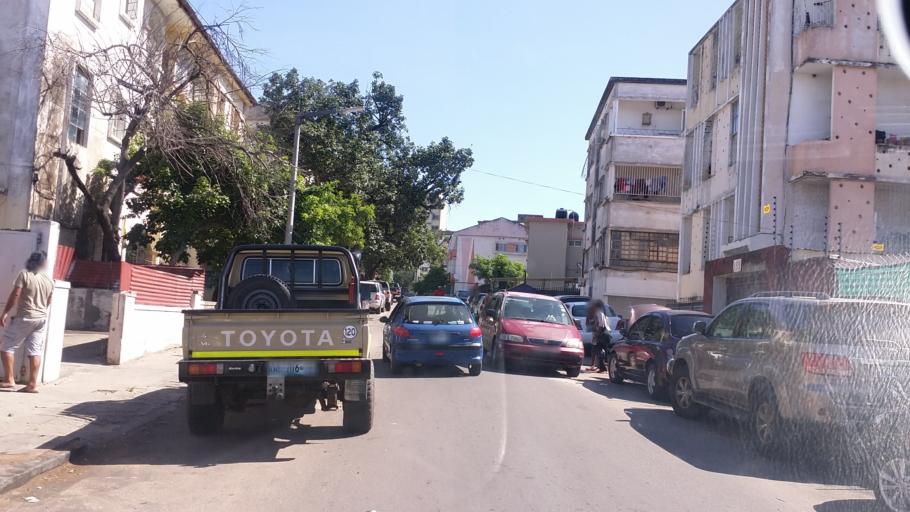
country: MZ
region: Maputo City
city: Maputo
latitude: -25.9593
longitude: 32.5778
